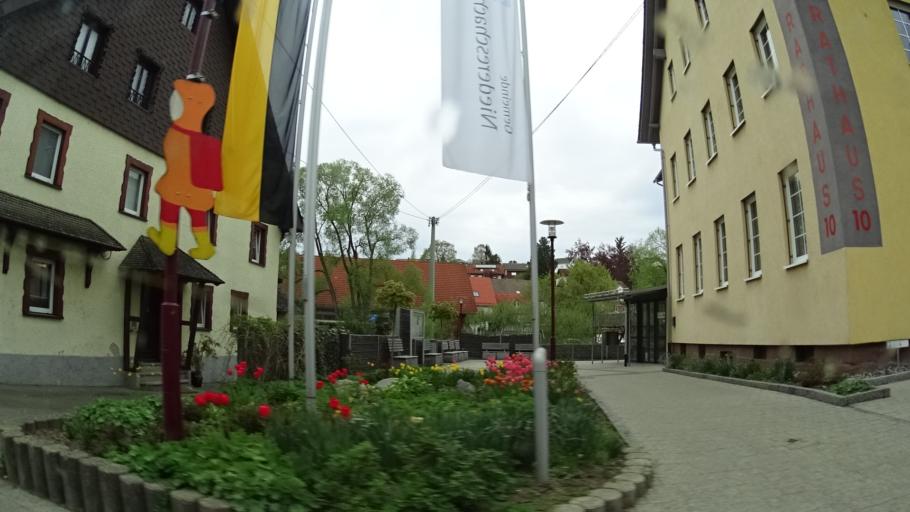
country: DE
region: Baden-Wuerttemberg
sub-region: Freiburg Region
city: Niedereschach
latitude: 48.1322
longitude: 8.5281
